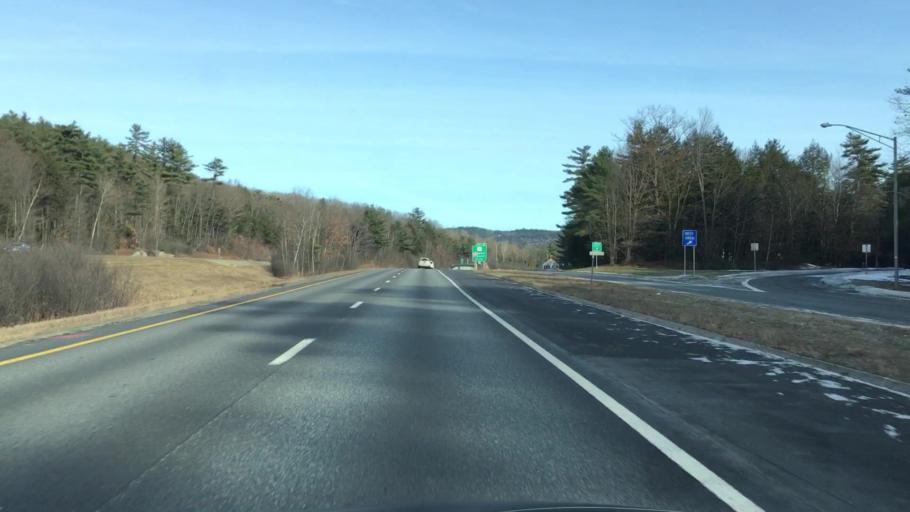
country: US
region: New Hampshire
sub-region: Grafton County
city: Lebanon
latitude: 43.6482
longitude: -72.2637
